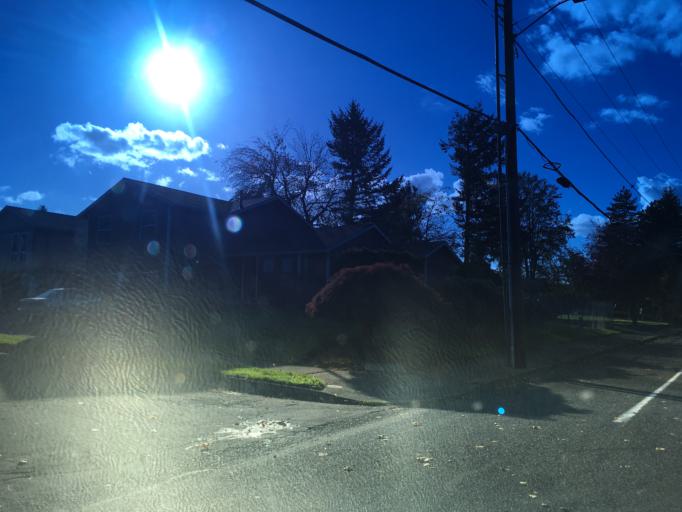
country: US
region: Oregon
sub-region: Multnomah County
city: Troutdale
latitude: 45.5096
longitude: -122.3950
